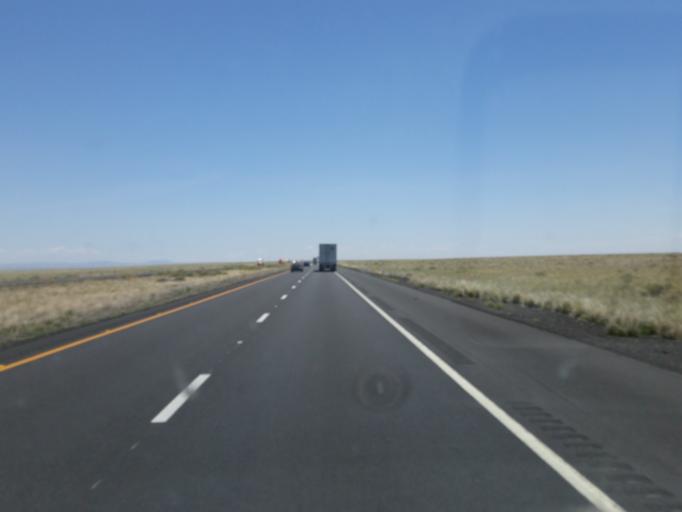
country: US
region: Arizona
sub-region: Coconino County
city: LeChee
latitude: 35.1198
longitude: -111.1490
